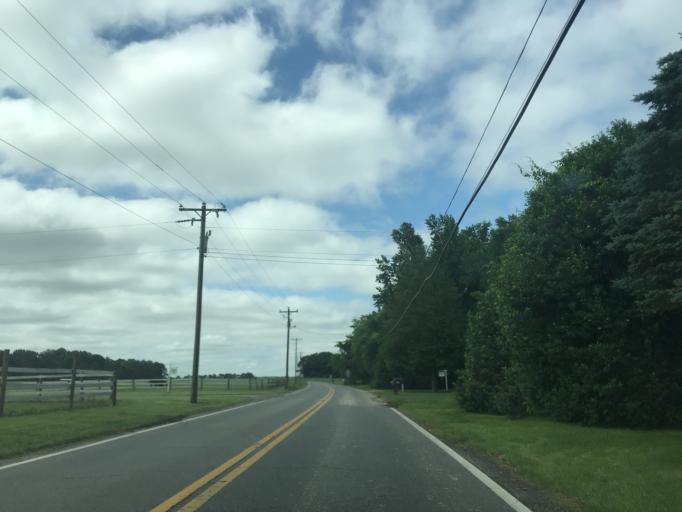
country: US
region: Maryland
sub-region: Caroline County
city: Ridgely
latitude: 38.8884
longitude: -75.9610
